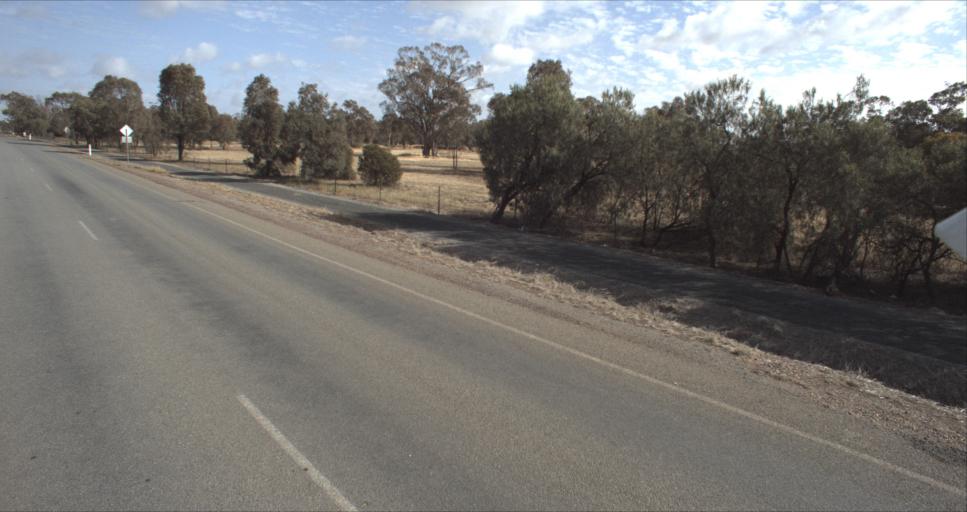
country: AU
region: New South Wales
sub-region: Leeton
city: Leeton
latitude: -34.5714
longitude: 146.4083
